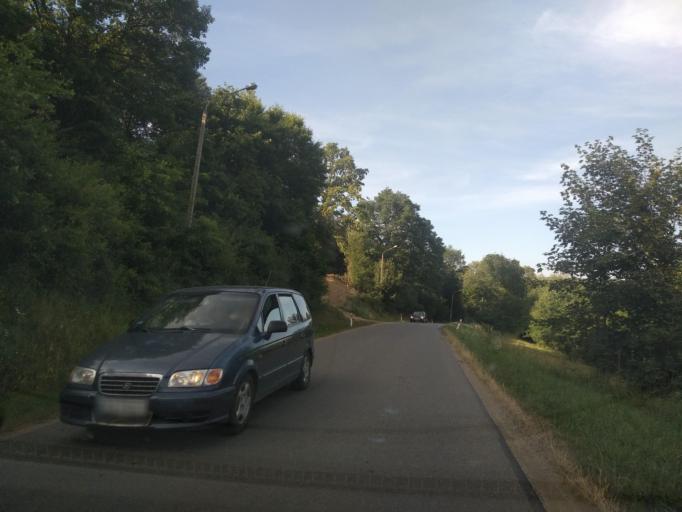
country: PL
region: Subcarpathian Voivodeship
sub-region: Powiat sanocki
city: Poraz
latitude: 49.4824
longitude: 22.2019
